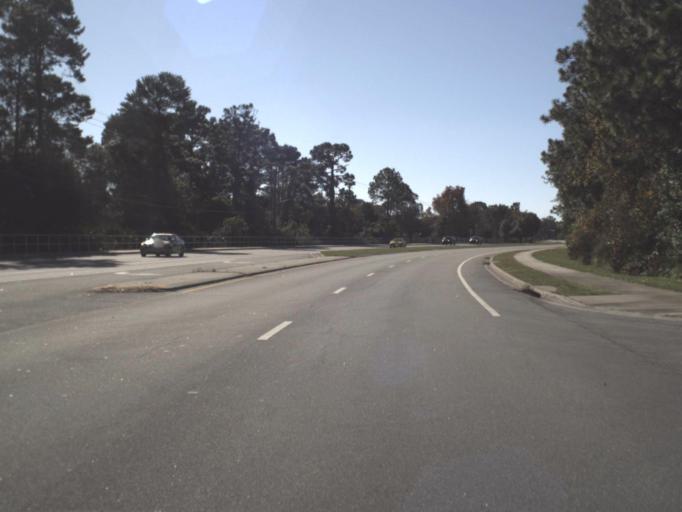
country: US
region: Florida
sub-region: Volusia County
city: Ormond Beach
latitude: 29.2672
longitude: -81.0941
